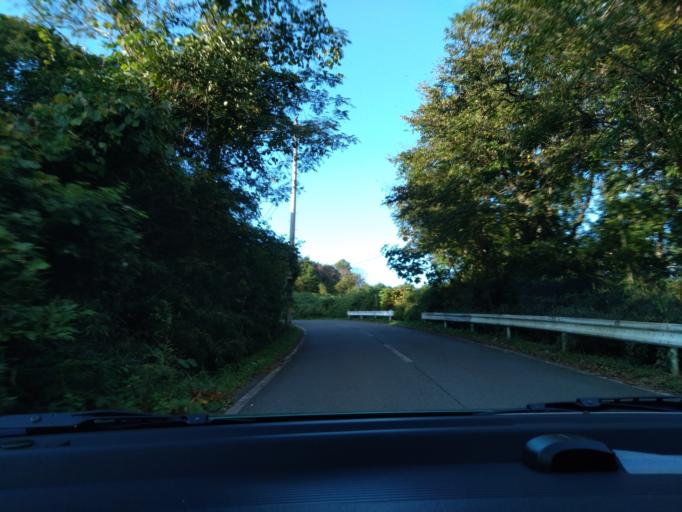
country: JP
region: Iwate
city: Ichinoseki
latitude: 38.8773
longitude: 141.1621
